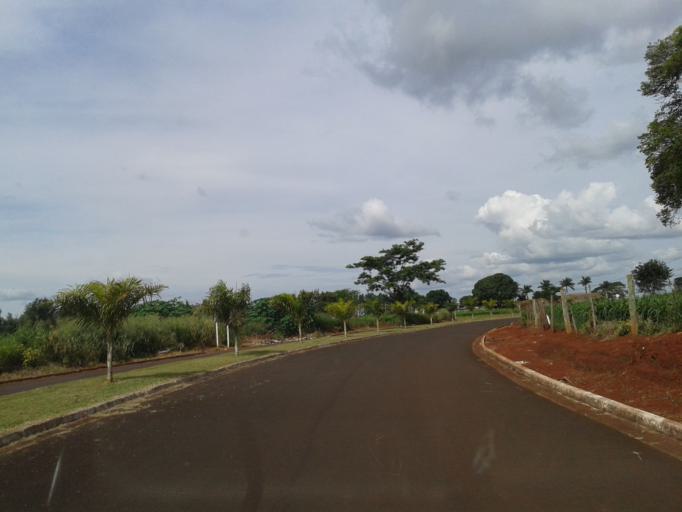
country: BR
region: Minas Gerais
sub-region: Centralina
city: Centralina
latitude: -18.5788
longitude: -49.1971
